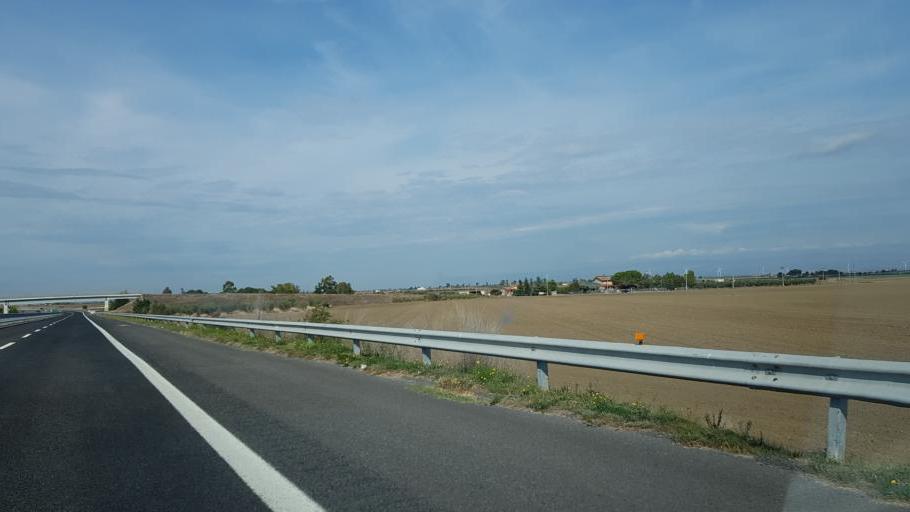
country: IT
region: Apulia
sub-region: Provincia di Foggia
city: Carapelle
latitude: 41.3812
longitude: 15.7525
